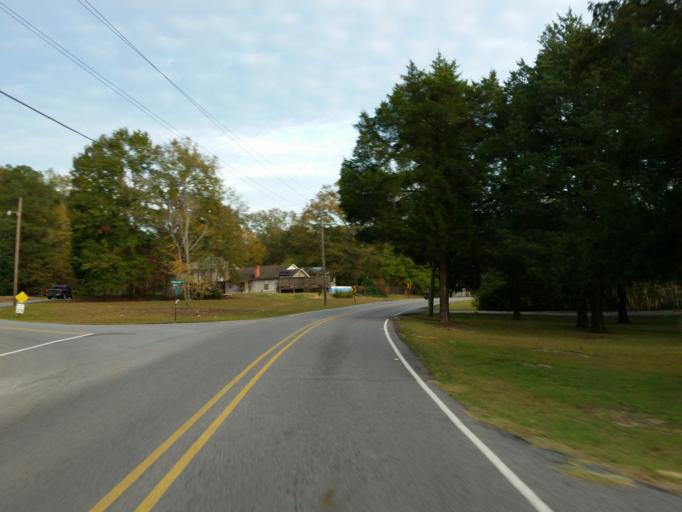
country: US
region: Mississippi
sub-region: Lauderdale County
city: Marion
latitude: 32.4116
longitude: -88.6110
